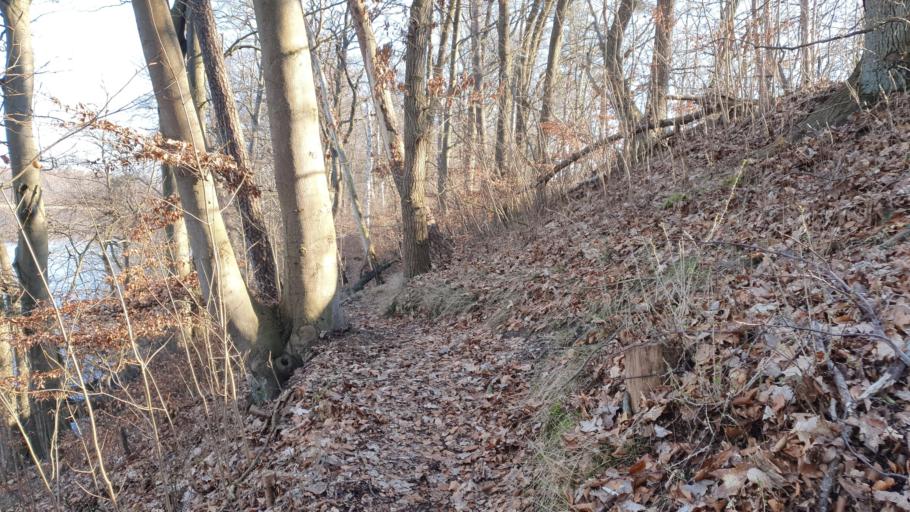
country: DE
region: Mecklenburg-Vorpommern
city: Wittenforden
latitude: 53.6426
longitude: 11.3344
